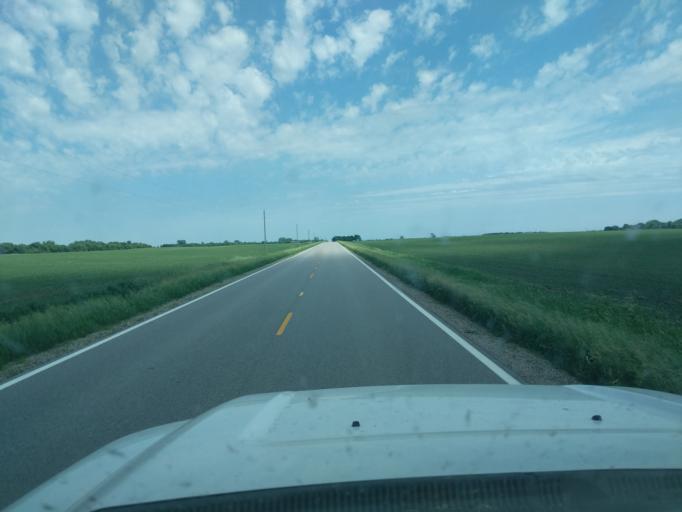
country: US
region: Minnesota
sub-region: Yellow Medicine County
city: Granite Falls
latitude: 44.7501
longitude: -95.4016
